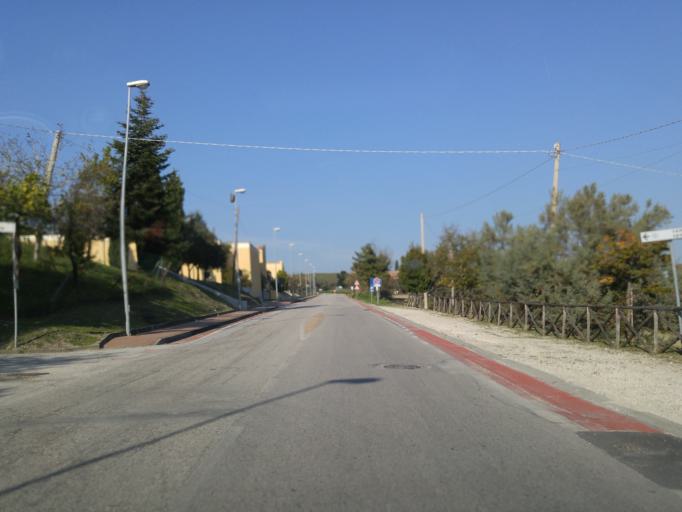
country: IT
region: The Marches
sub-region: Provincia di Pesaro e Urbino
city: Piagge
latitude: 43.7377
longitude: 12.9698
